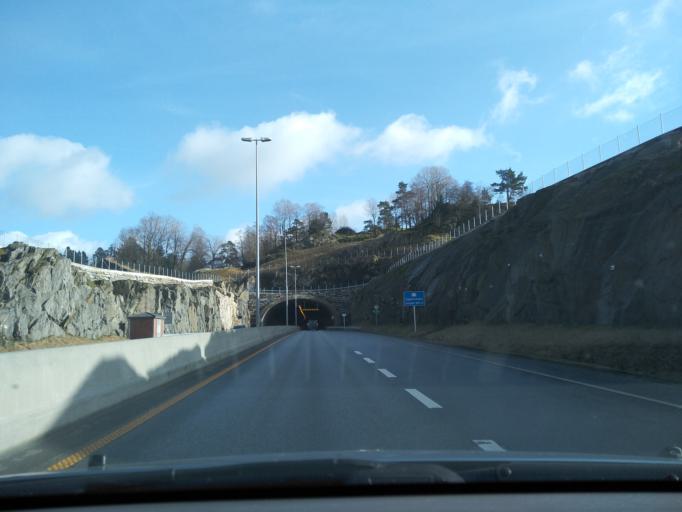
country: NO
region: Rogaland
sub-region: Tysvaer
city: Aksdal
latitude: 59.5069
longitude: 5.6120
